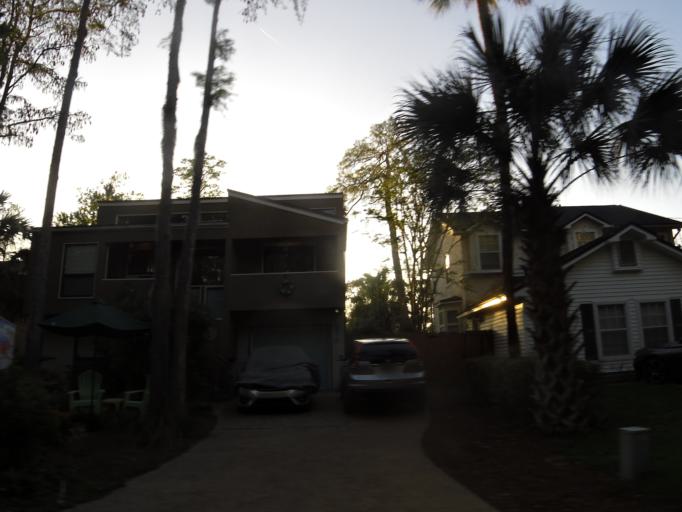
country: US
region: Florida
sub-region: Duval County
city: Atlantic Beach
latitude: 30.3299
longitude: -81.4027
